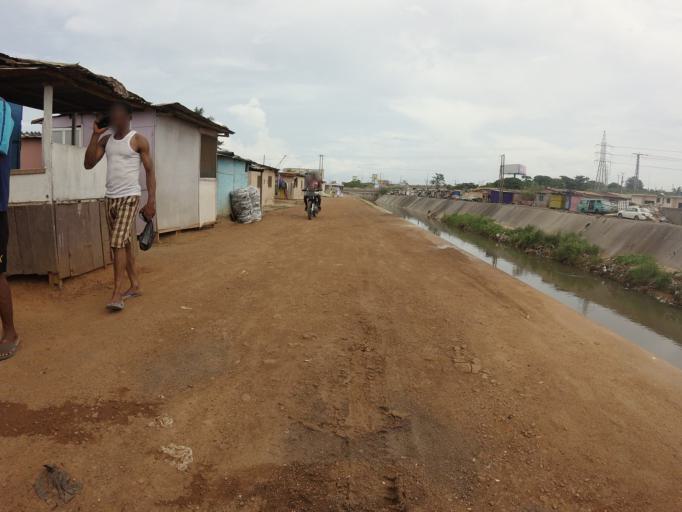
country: GH
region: Greater Accra
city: Accra
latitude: 5.5926
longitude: -0.2178
